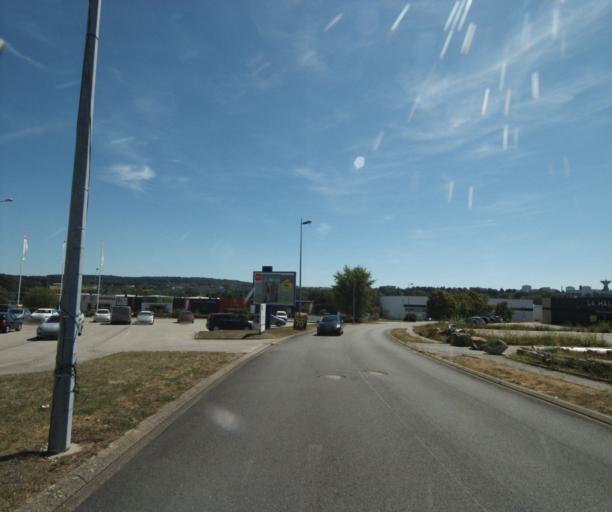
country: FR
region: Lorraine
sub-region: Departement des Vosges
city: Epinal
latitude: 48.1984
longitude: 6.4684
